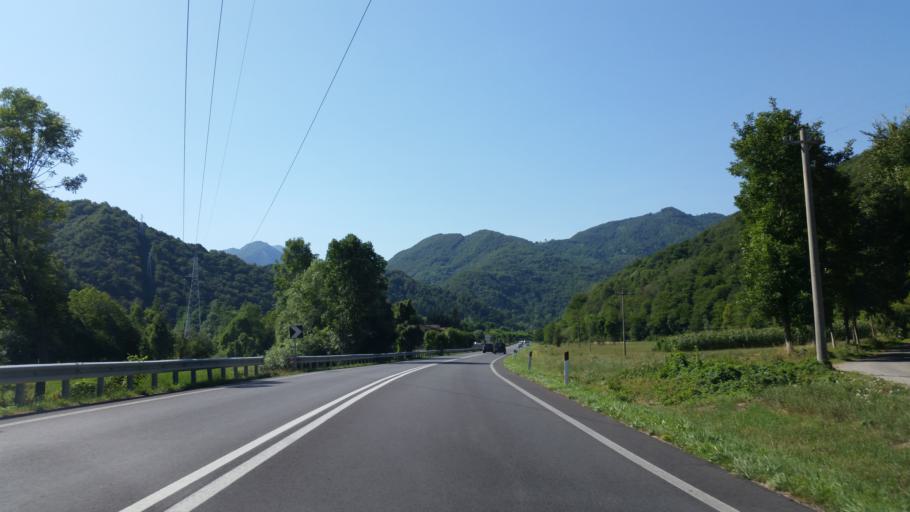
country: IT
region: Piedmont
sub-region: Provincia di Cuneo
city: Robilante
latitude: 44.2741
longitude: 7.5191
